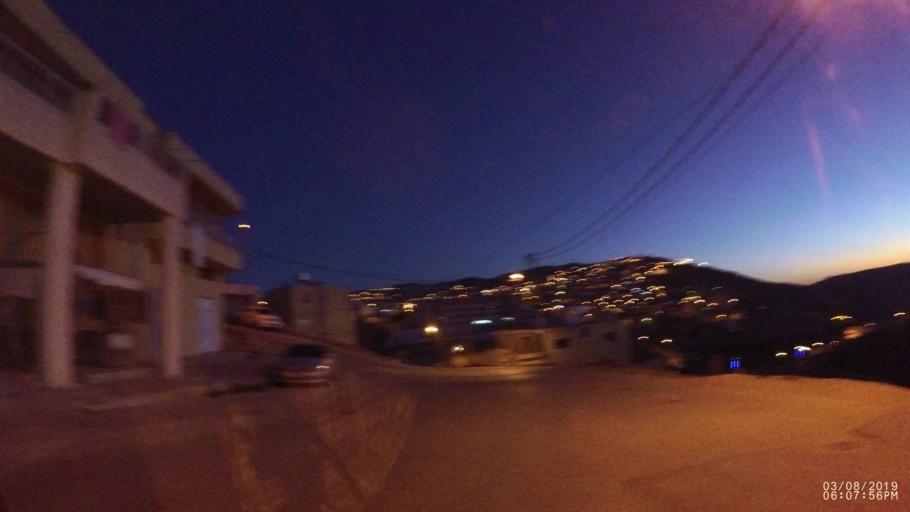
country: JO
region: Ma'an
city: Petra
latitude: 30.3282
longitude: 35.4765
